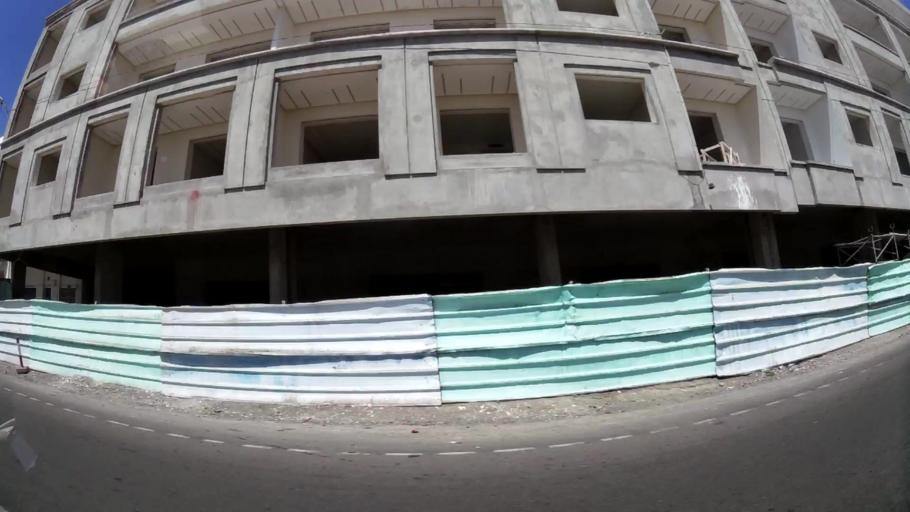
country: MA
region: Souss-Massa-Draa
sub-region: Agadir-Ida-ou-Tnan
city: Agadir
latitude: 30.4263
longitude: -9.6161
